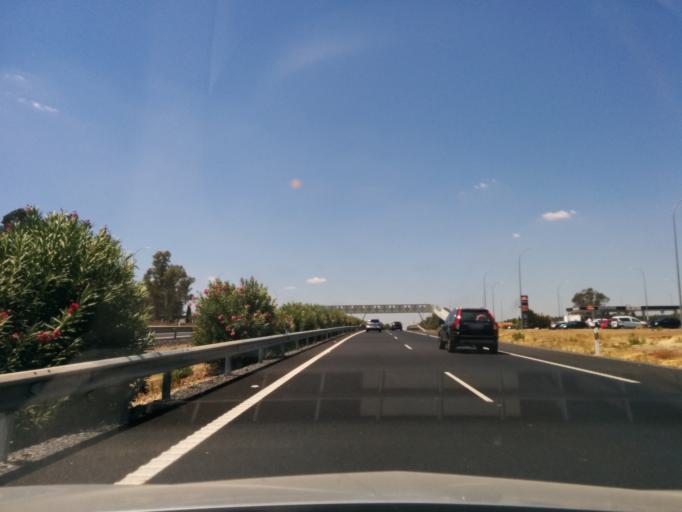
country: ES
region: Andalusia
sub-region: Provincia de Huelva
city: Chucena
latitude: 37.3484
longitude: -6.4210
